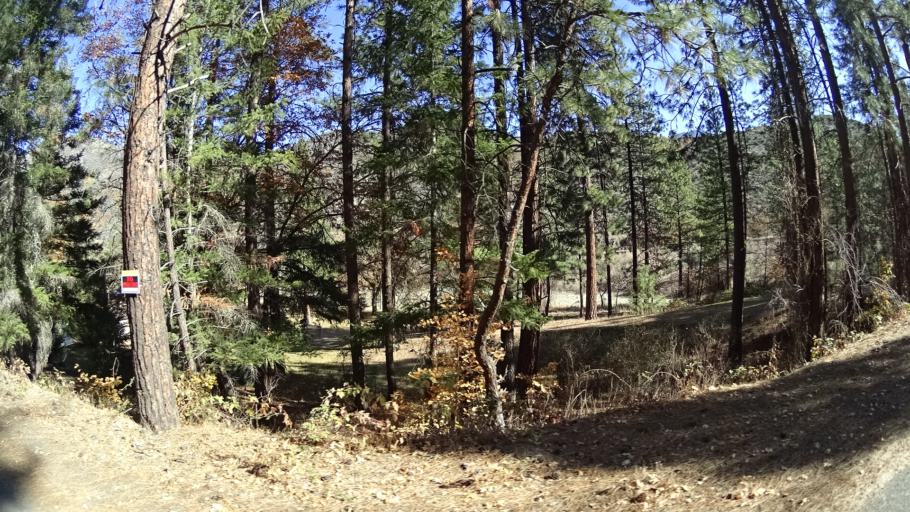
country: US
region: California
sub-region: Siskiyou County
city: Yreka
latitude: 41.8606
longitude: -122.7067
